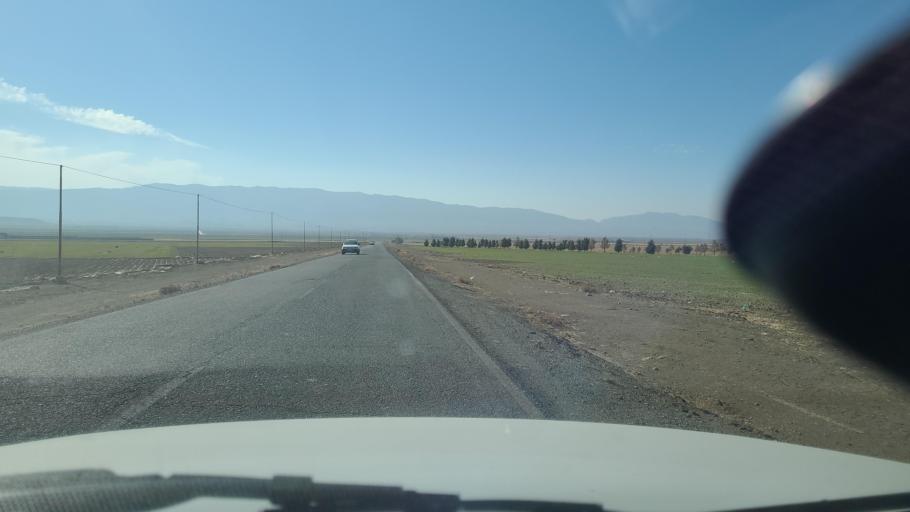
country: IR
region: Razavi Khorasan
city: Dowlatabad
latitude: 35.6059
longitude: 59.4646
